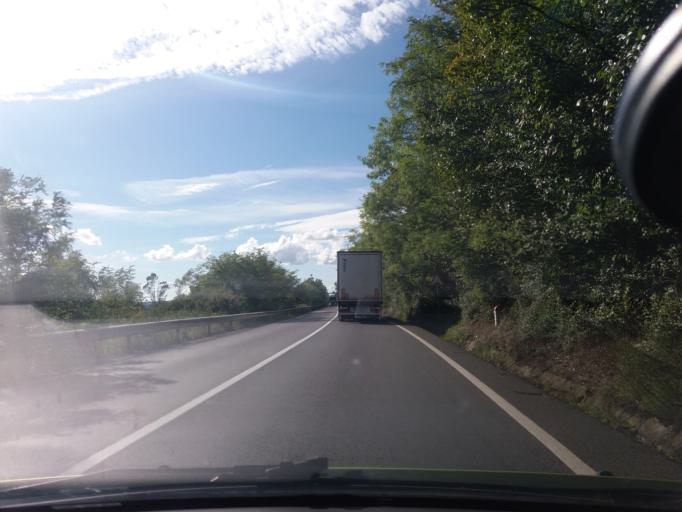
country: RO
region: Arad
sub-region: Comuna Varadia de Mures
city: Varadia de Mures
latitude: 46.0307
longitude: 22.1109
